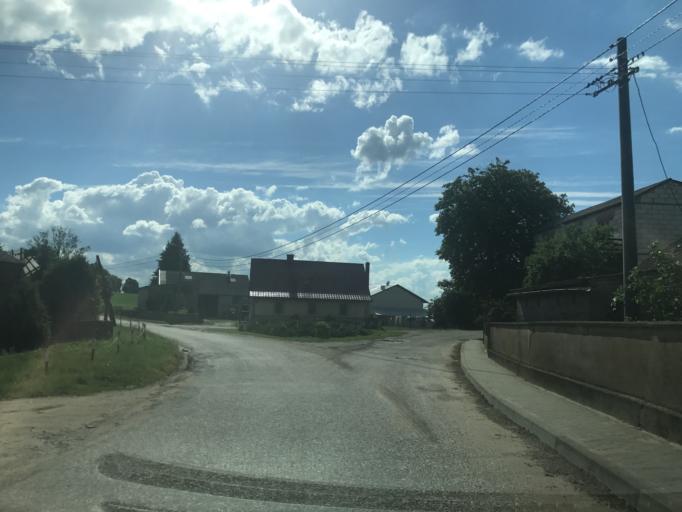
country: PL
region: Kujawsko-Pomorskie
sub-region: Powiat brodnicki
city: Brzozie
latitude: 53.3548
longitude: 19.6030
